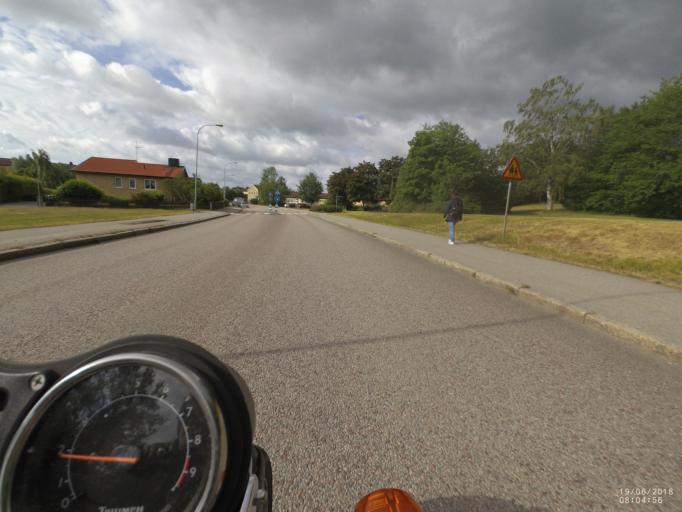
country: SE
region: Soedermanland
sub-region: Nykopings Kommun
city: Nykoping
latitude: 58.7713
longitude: 16.9794
